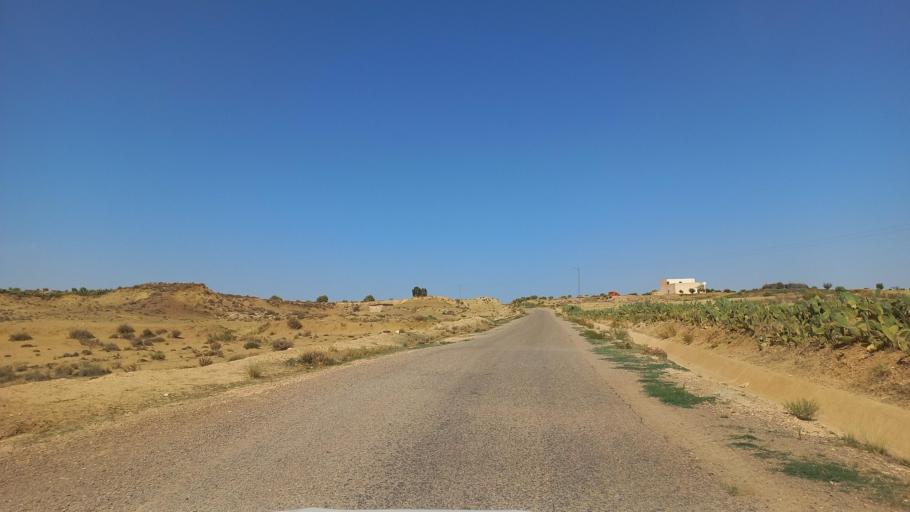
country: TN
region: Al Qasrayn
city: Kasserine
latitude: 35.2069
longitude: 9.0387
